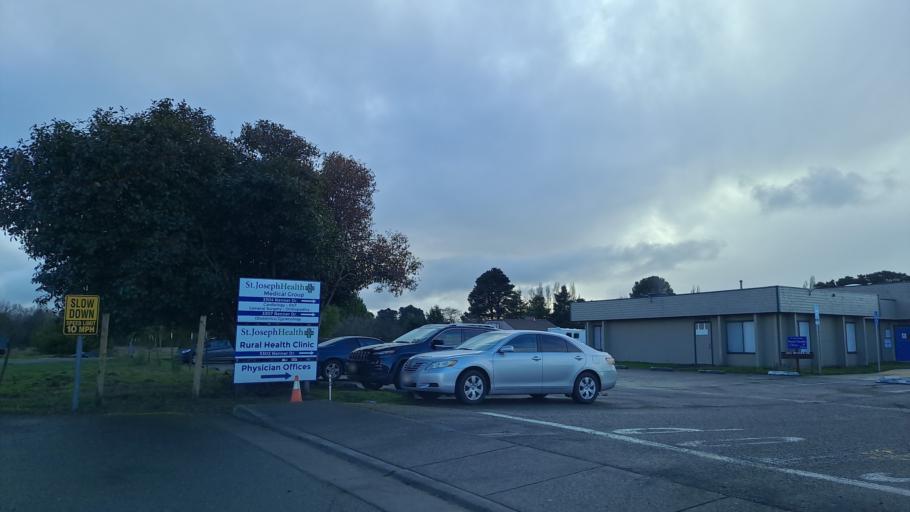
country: US
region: California
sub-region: Humboldt County
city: Fortuna
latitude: 40.5817
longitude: -124.1356
